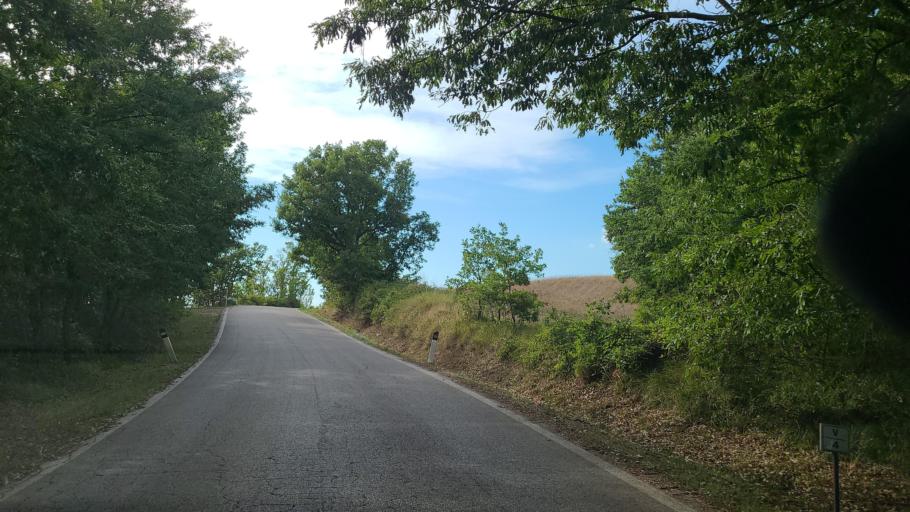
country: IT
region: Tuscany
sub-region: Provincia di Siena
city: San Gimignano
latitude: 43.4367
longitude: 10.9627
